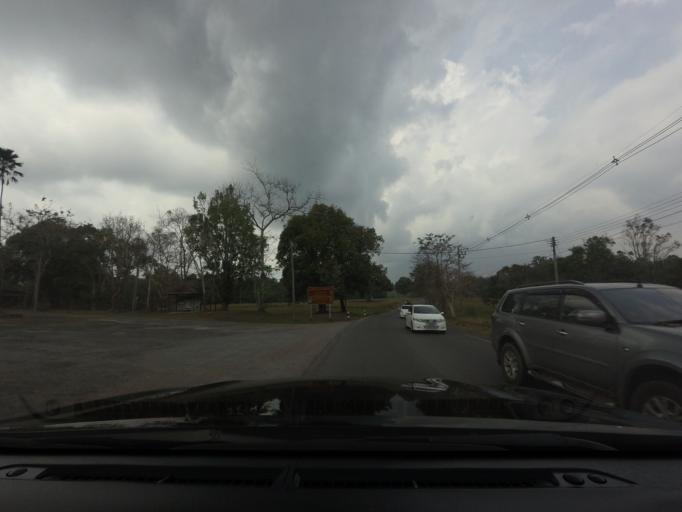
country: TH
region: Nakhon Nayok
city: Nakhon Nayok
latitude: 14.4111
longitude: 101.3715
